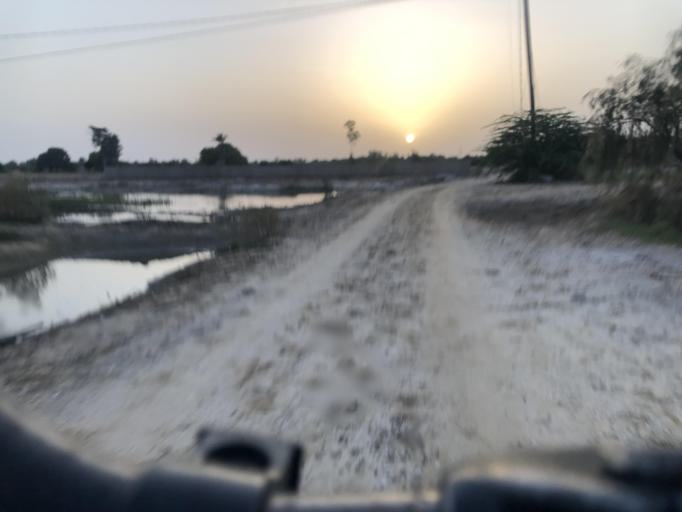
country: SN
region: Saint-Louis
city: Saint-Louis
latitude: 16.0720
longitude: -16.4330
